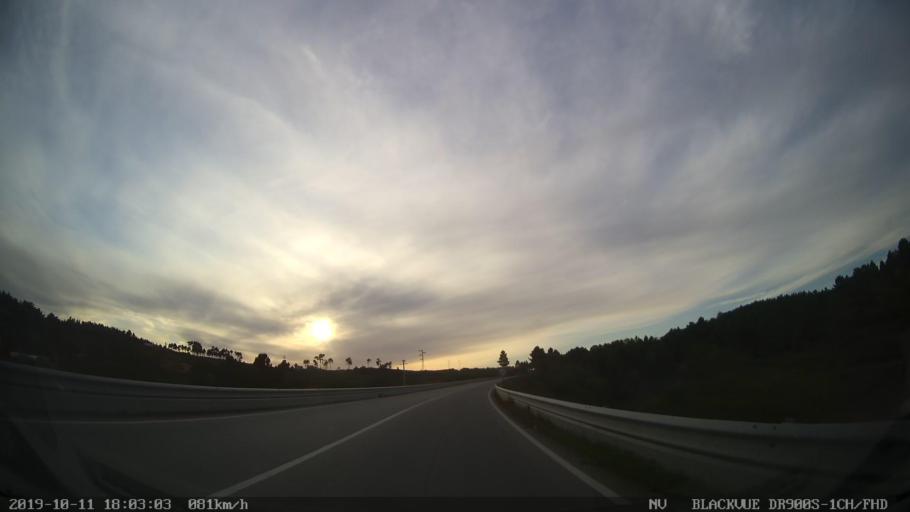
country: PT
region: Vila Real
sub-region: Sabrosa
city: Sabrosa
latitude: 41.2606
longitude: -7.6025
